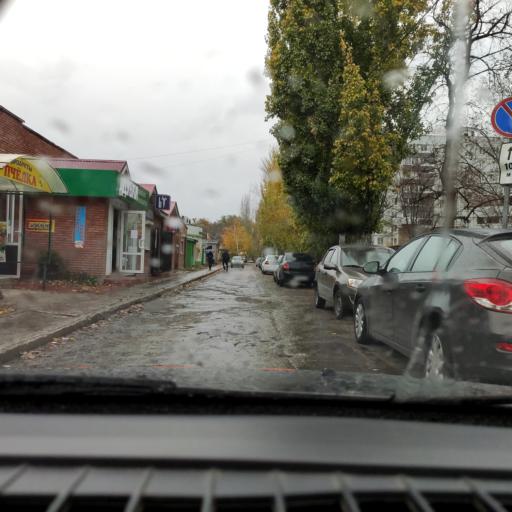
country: RU
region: Samara
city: Tol'yatti
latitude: 53.5100
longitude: 49.2639
